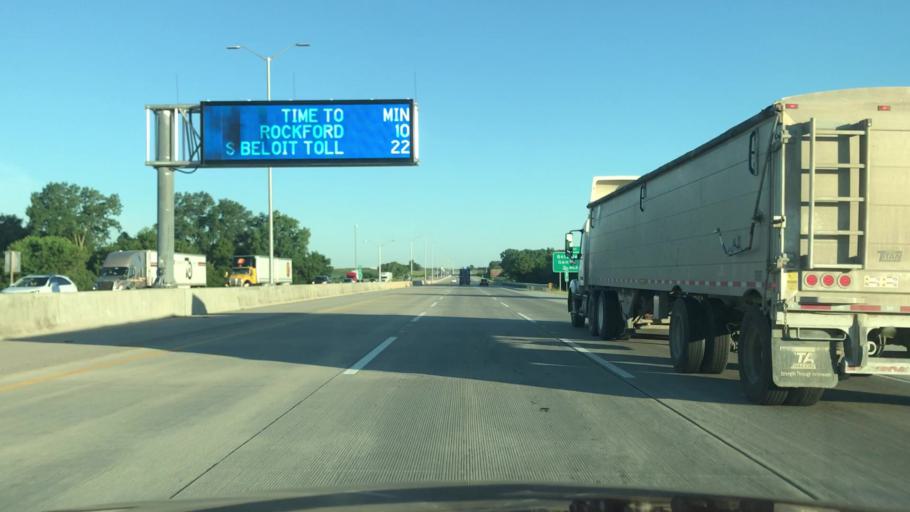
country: US
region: Illinois
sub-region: Boone County
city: Belvidere
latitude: 42.2280
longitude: -88.7706
